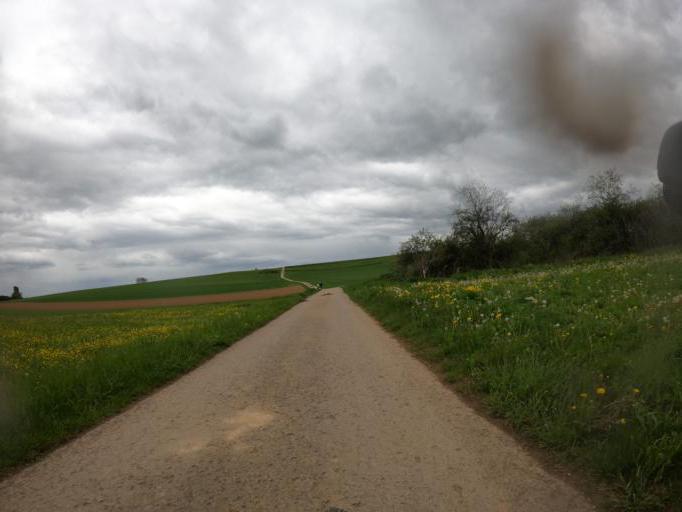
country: DE
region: Baden-Wuerttemberg
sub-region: Karlsruhe Region
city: Nagold
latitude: 48.5300
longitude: 8.7020
